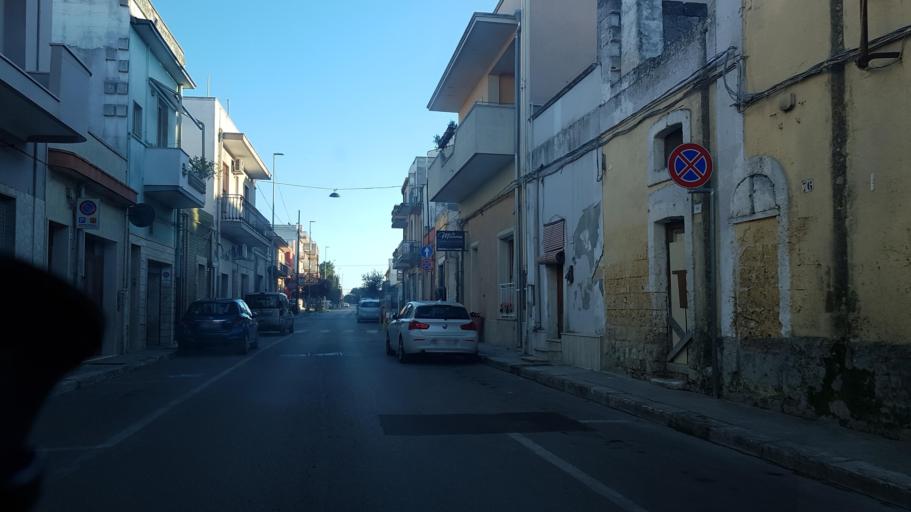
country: IT
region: Apulia
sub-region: Provincia di Brindisi
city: Latiano
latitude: 40.5496
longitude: 17.7186
